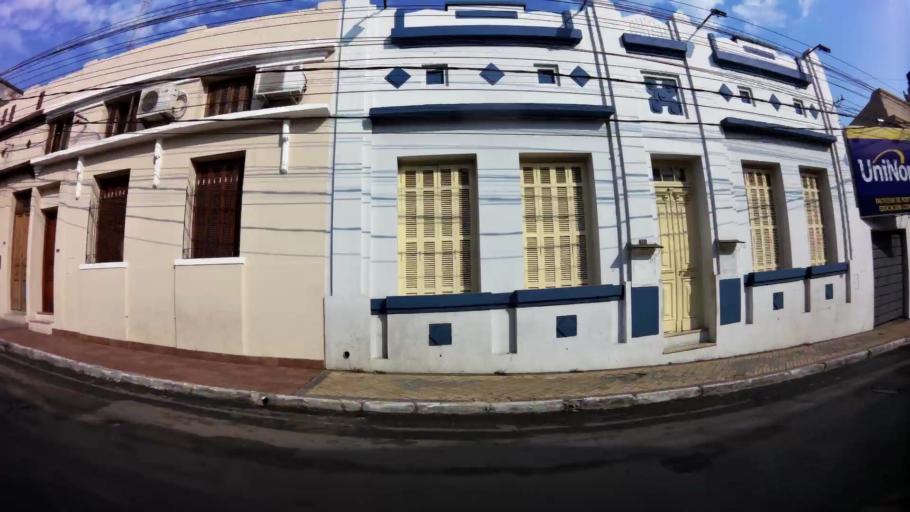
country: PY
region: Asuncion
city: Asuncion
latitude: -25.2865
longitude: -57.6232
